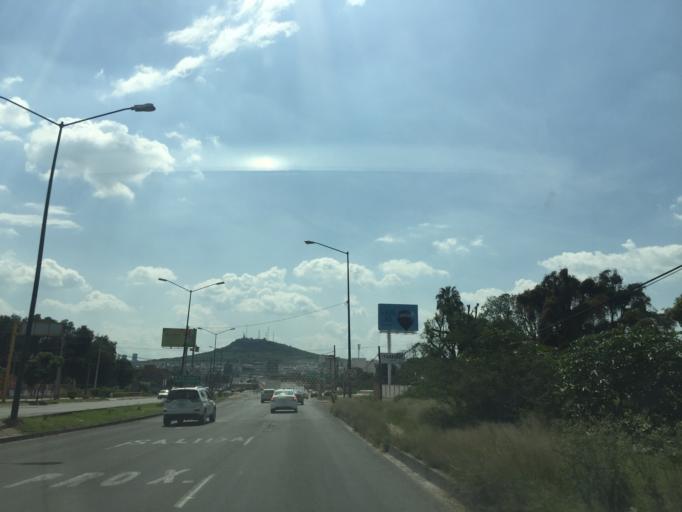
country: MX
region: Guanajuato
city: Leon
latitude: 21.1698
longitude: -101.6883
